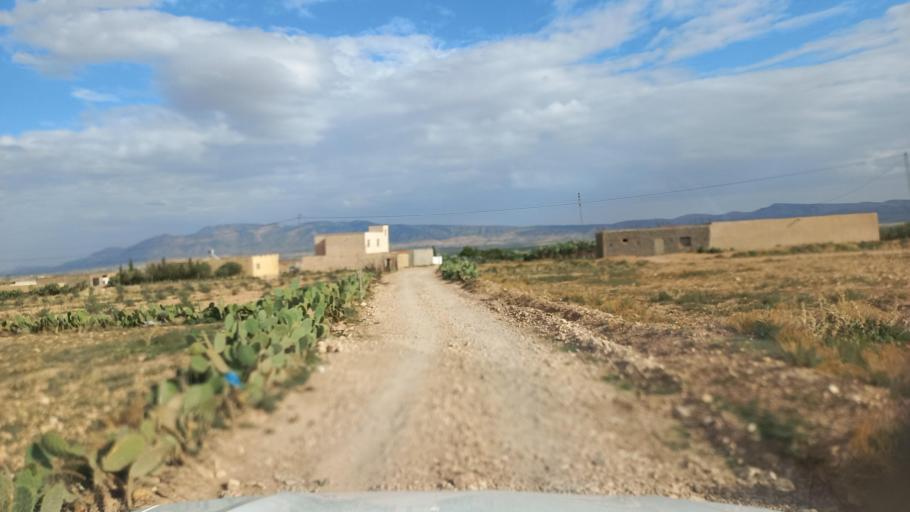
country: TN
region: Al Qasrayn
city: Sbiba
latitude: 35.4500
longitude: 9.0834
